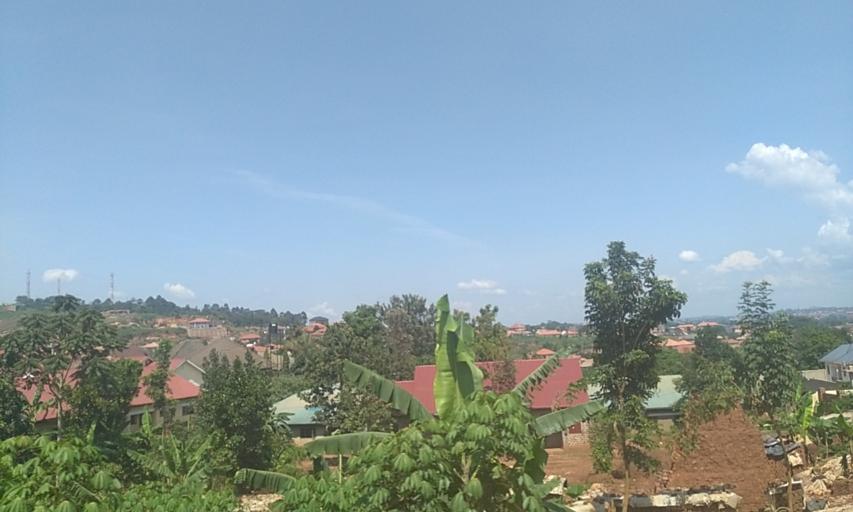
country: UG
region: Central Region
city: Kampala Central Division
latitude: 0.3823
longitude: 32.5957
